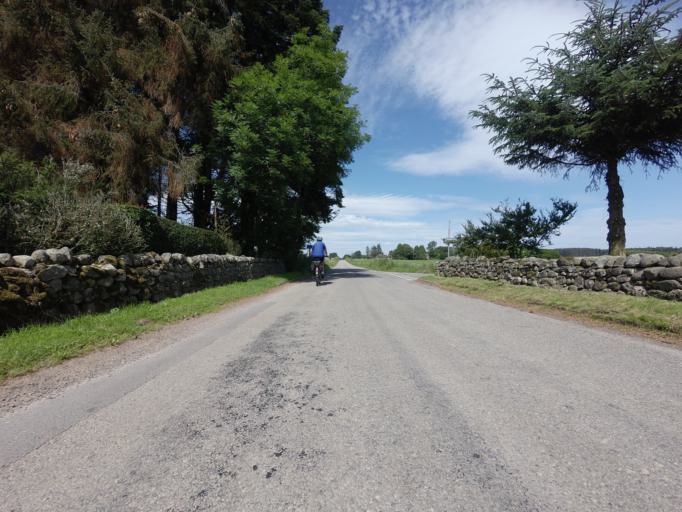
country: GB
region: Scotland
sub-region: Highland
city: Inverness
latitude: 57.5238
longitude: -4.3143
